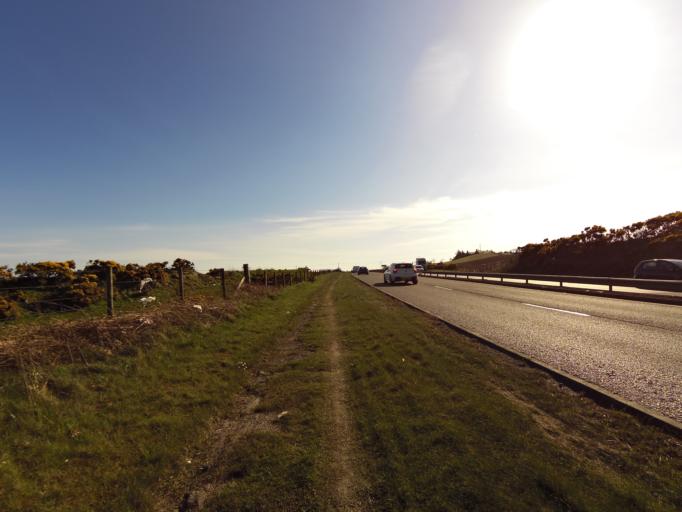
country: GB
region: Scotland
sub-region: Aberdeenshire
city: Newtonhill
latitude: 57.0047
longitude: -2.1747
